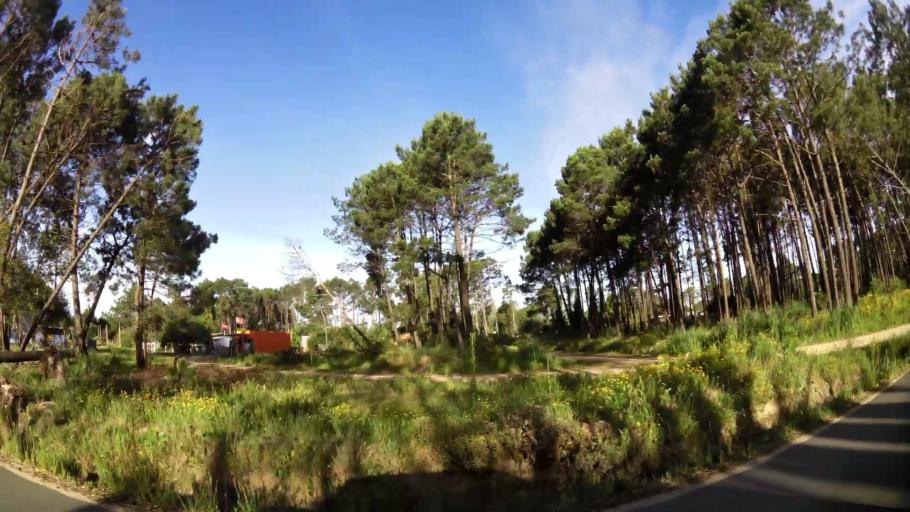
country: UY
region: Canelones
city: Empalme Olmos
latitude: -34.7698
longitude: -55.8579
